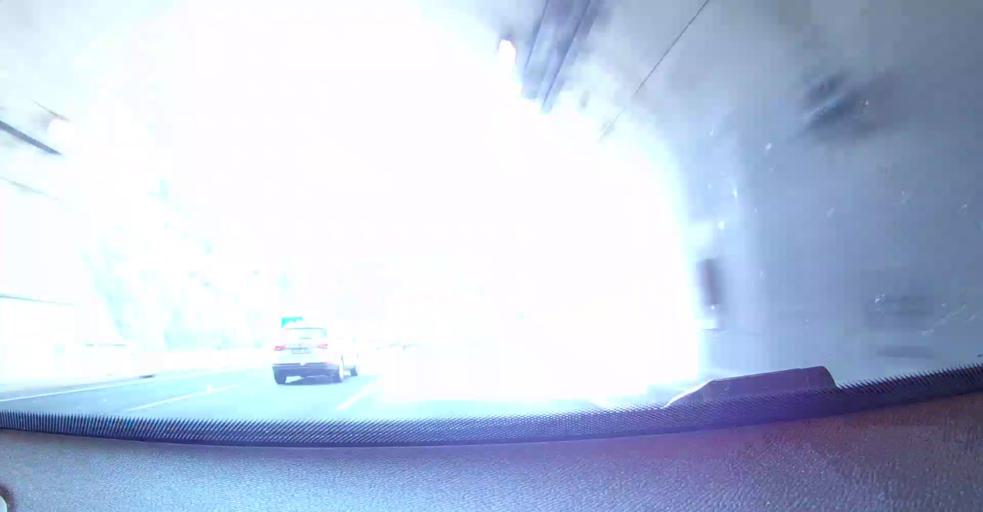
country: ES
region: Basque Country
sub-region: Provincia de Alava
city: Arminon
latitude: 42.7849
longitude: -2.8238
